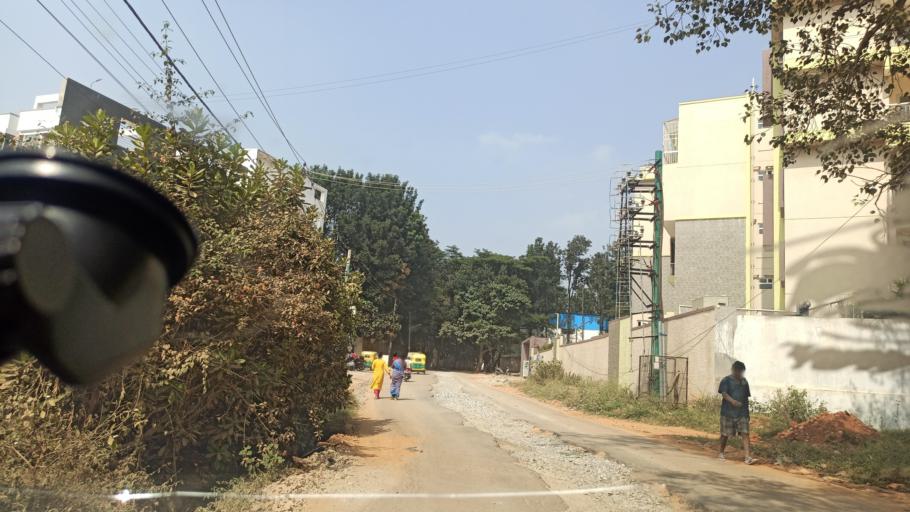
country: IN
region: Karnataka
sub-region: Bangalore Urban
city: Yelahanka
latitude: 13.0926
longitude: 77.6192
